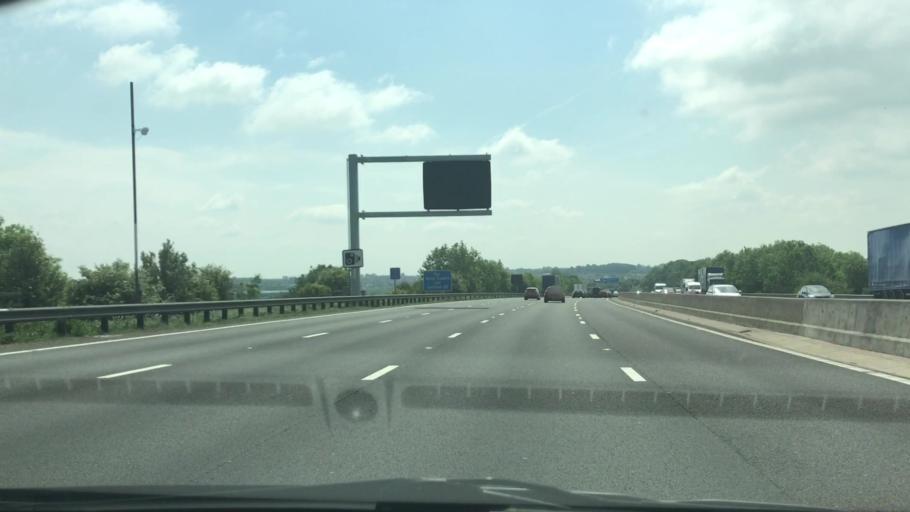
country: GB
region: England
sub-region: Derbyshire
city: Blackwell
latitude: 53.1263
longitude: -1.3299
